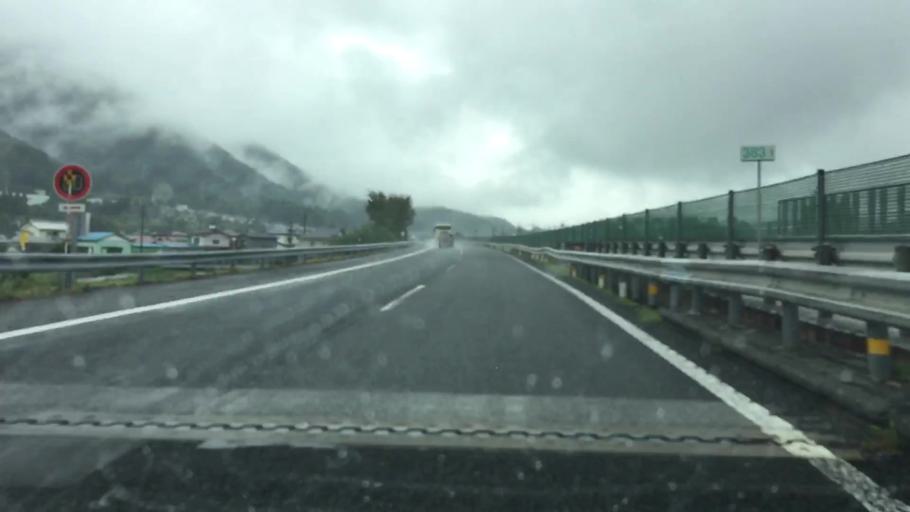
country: JP
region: Yamanashi
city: Otsuki
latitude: 35.5310
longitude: 138.8582
